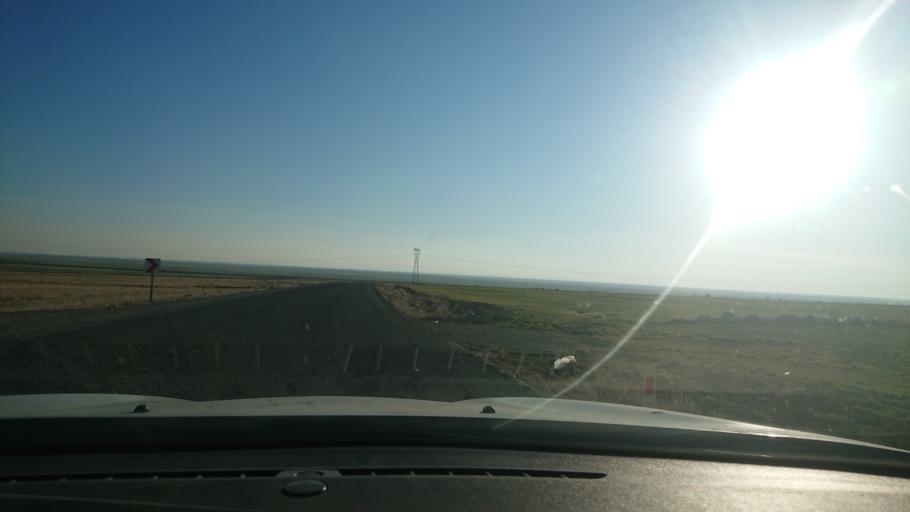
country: TR
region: Aksaray
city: Acipinar
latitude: 38.6748
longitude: 33.7300
